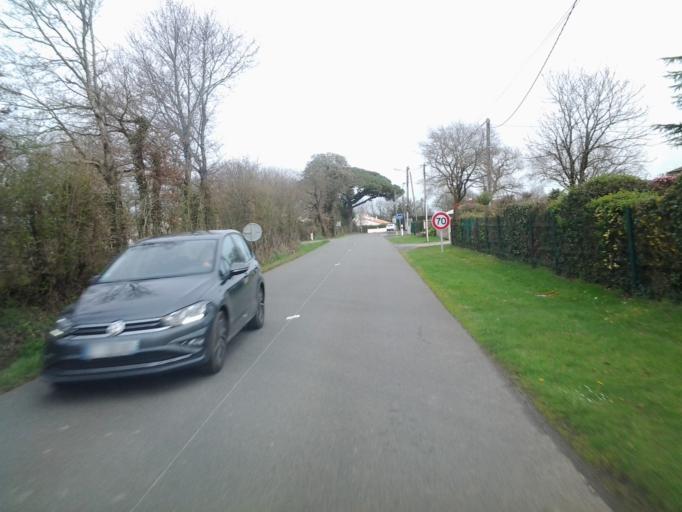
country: FR
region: Pays de la Loire
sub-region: Departement de la Vendee
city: Avrille
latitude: 46.4999
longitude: -1.4584
